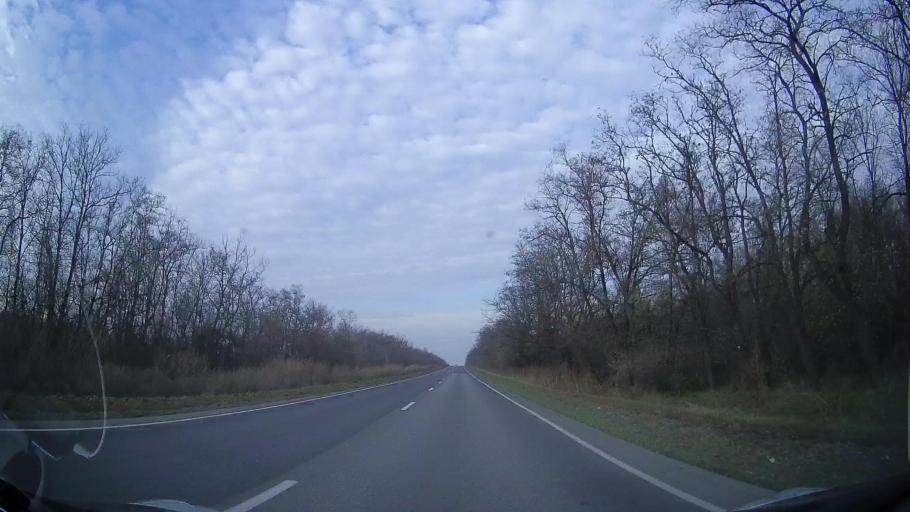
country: RU
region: Rostov
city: Bagayevskaya
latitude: 47.1201
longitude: 40.2767
